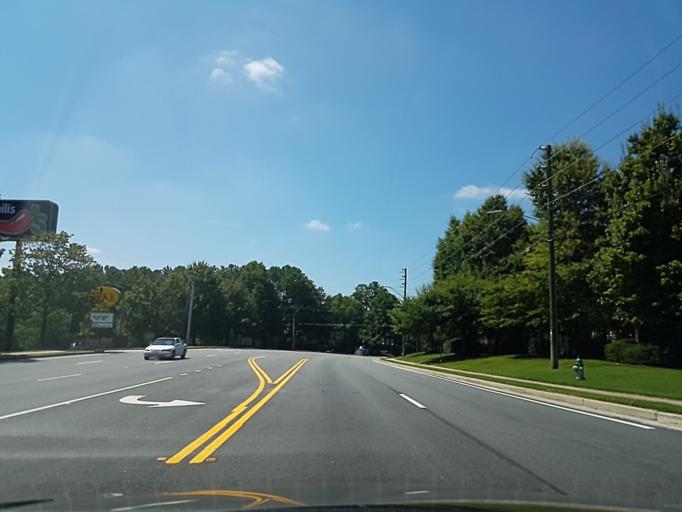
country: US
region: Georgia
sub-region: DeKalb County
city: North Druid Hills
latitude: 33.8169
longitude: -84.3162
